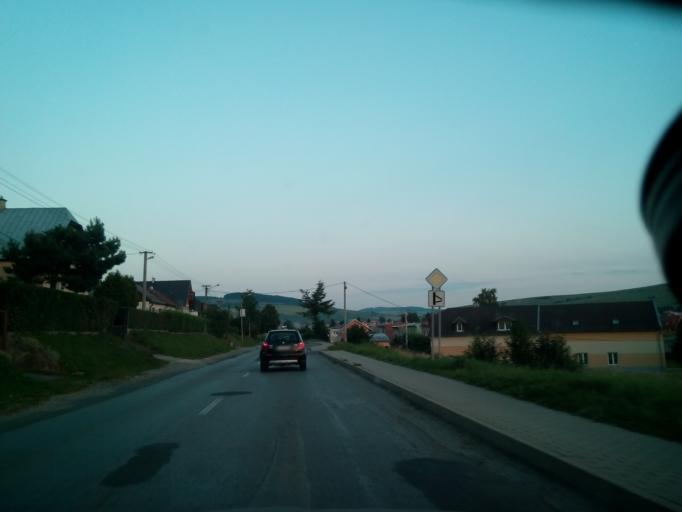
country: SK
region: Presovsky
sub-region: Okres Presov
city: Kezmarok
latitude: 49.1261
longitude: 20.4376
